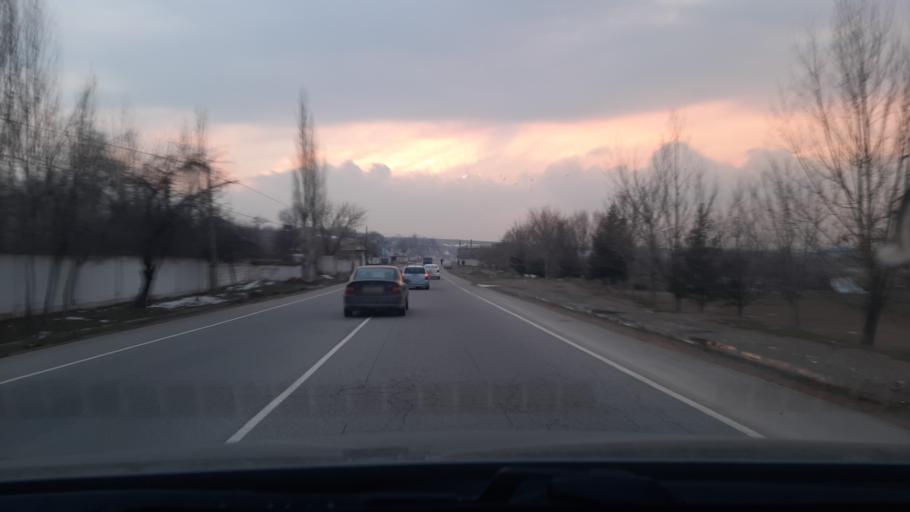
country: TJ
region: Republican Subordination
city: Vahdat
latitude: 38.5136
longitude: 69.0784
